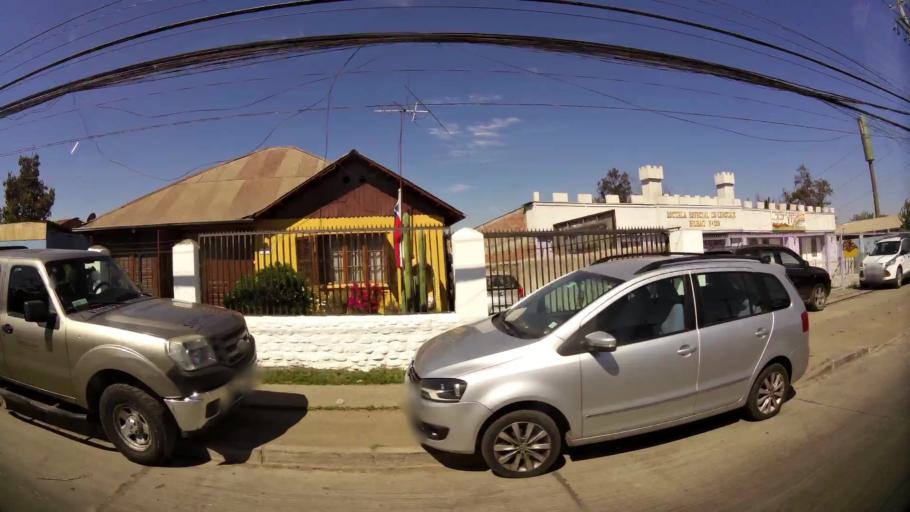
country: CL
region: Santiago Metropolitan
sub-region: Provincia de Talagante
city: Penaflor
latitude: -33.6076
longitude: -70.8791
